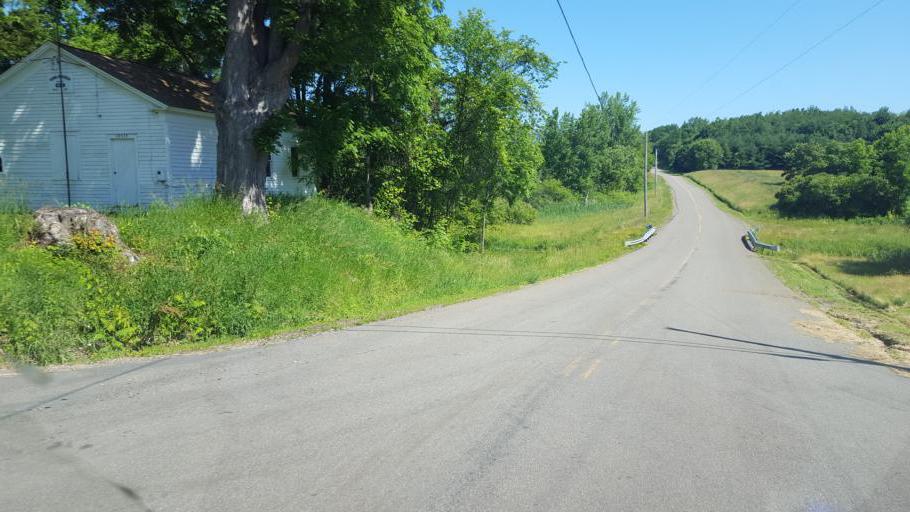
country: US
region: New York
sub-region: Wayne County
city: Wolcott
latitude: 43.2640
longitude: -76.8843
